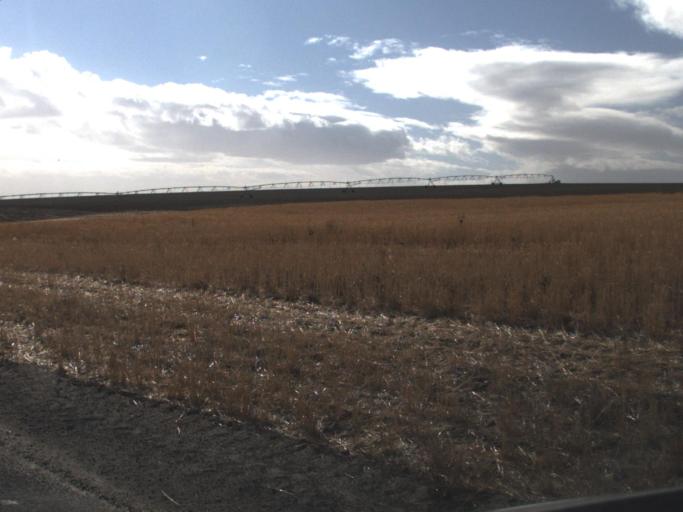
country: US
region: Washington
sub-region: Okanogan County
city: Coulee Dam
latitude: 47.5878
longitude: -118.7861
